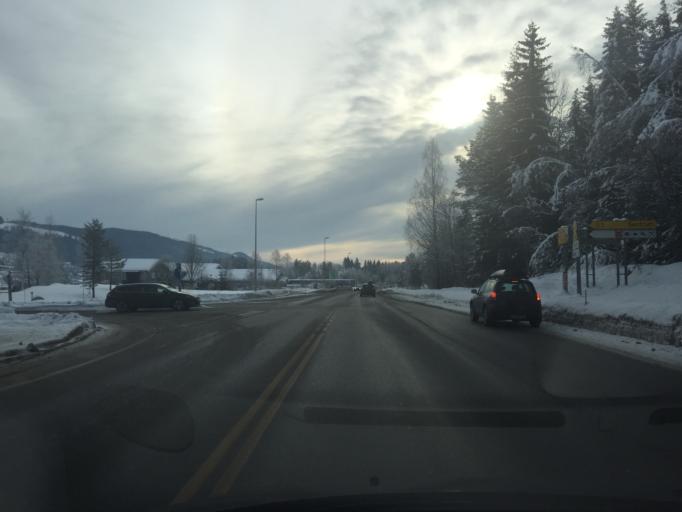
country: NO
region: Hedmark
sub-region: Trysil
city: Innbygda
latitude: 61.3165
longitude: 12.2527
